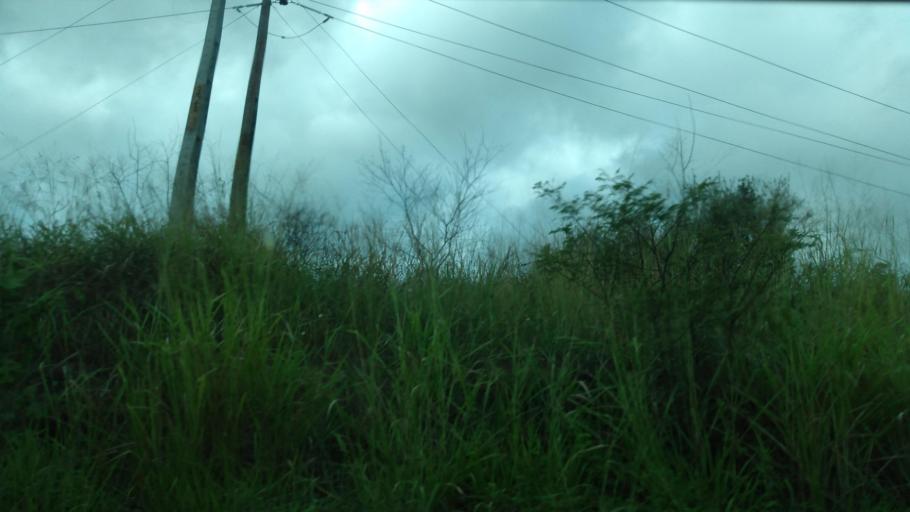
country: BR
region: Pernambuco
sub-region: Caruaru
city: Caruaru
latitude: -8.3175
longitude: -35.9793
